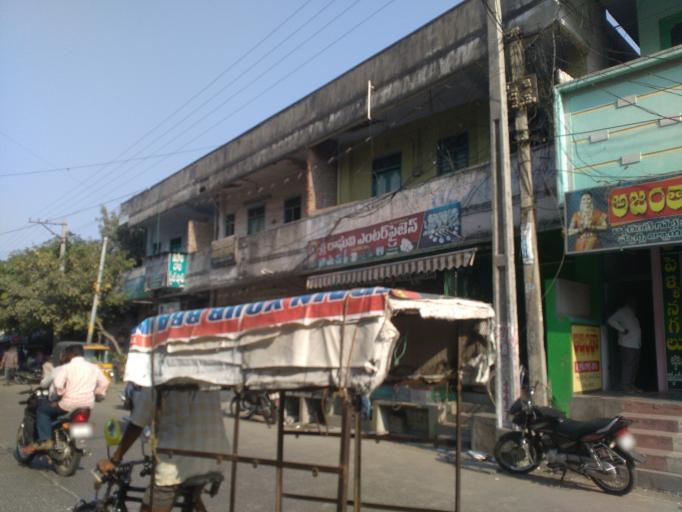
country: IN
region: Andhra Pradesh
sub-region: Prakasam
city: Chirala
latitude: 15.8254
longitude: 80.3534
